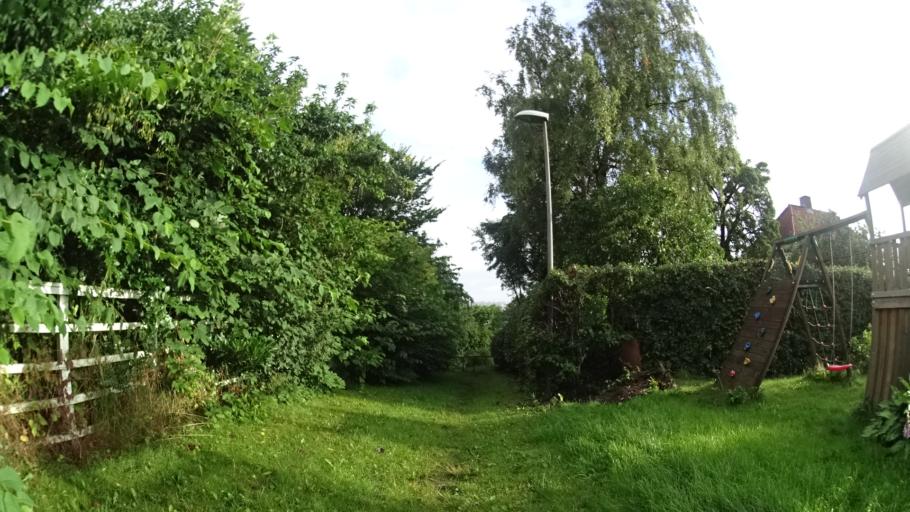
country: DK
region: Central Jutland
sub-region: Arhus Kommune
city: Stavtrup
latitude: 56.1228
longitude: 10.1626
